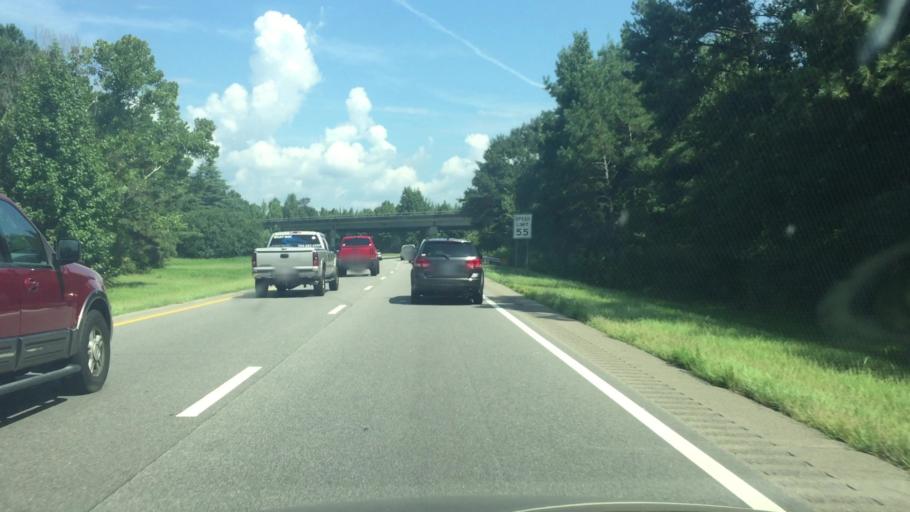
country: US
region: North Carolina
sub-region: Scotland County
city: Laurinburg
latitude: 34.7860
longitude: -79.5038
